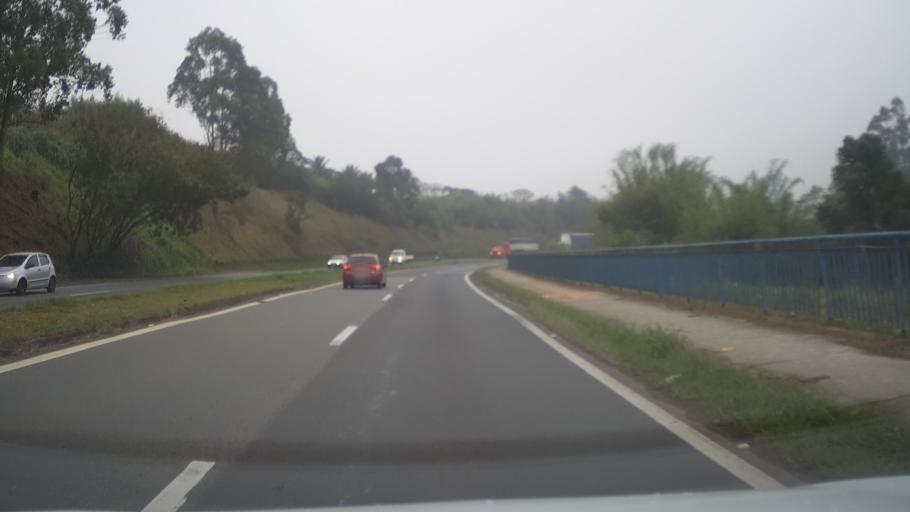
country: BR
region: Sao Paulo
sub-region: Itatiba
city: Itatiba
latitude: -23.0293
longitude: -46.8417
